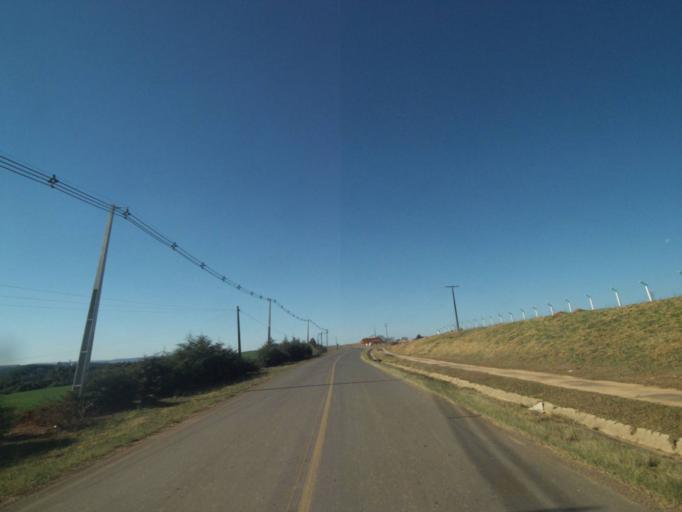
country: BR
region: Parana
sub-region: Tibagi
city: Tibagi
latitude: -24.5257
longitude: -50.4367
